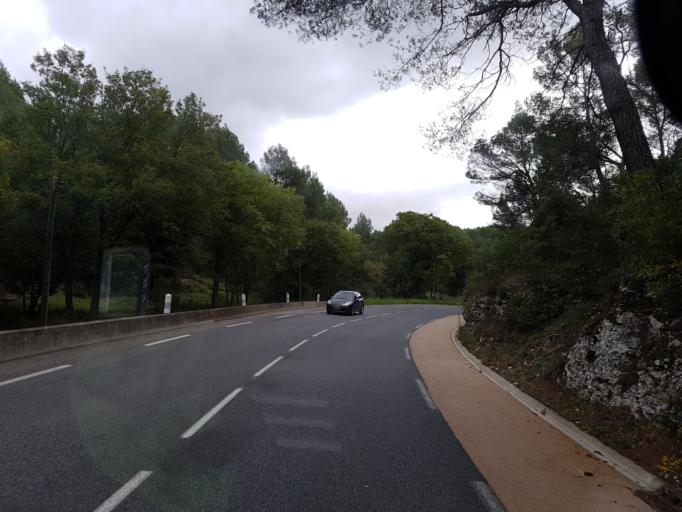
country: FR
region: Provence-Alpes-Cote d'Azur
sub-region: Departement des Bouches-du-Rhone
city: Cuges-les-Pins
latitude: 43.2656
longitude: 5.7396
